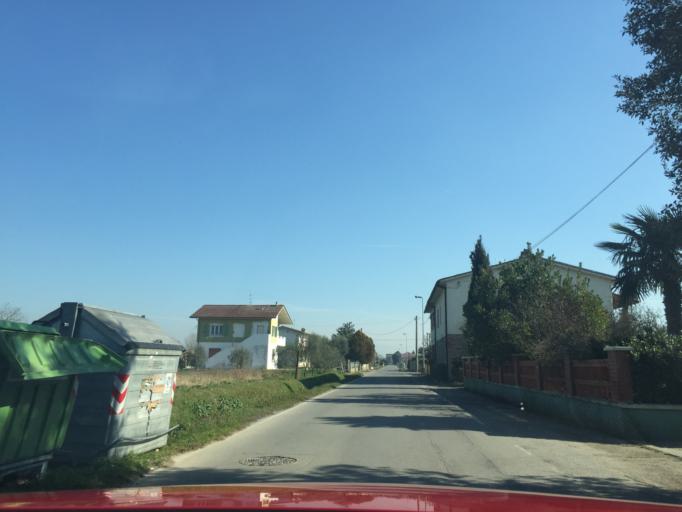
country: IT
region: Tuscany
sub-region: Provincia di Pistoia
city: Anchione
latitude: 43.8246
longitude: 10.7474
